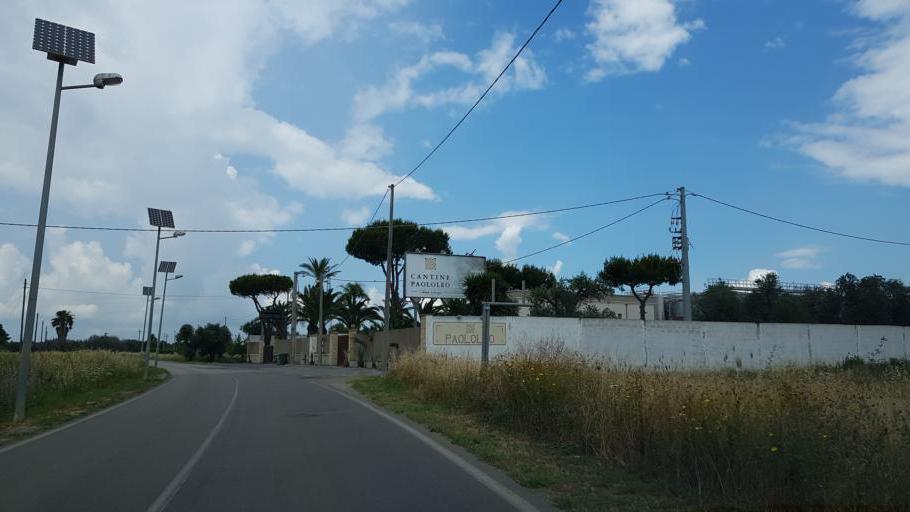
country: IT
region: Apulia
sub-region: Provincia di Brindisi
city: San Donaci
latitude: 40.4567
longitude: 17.9232
